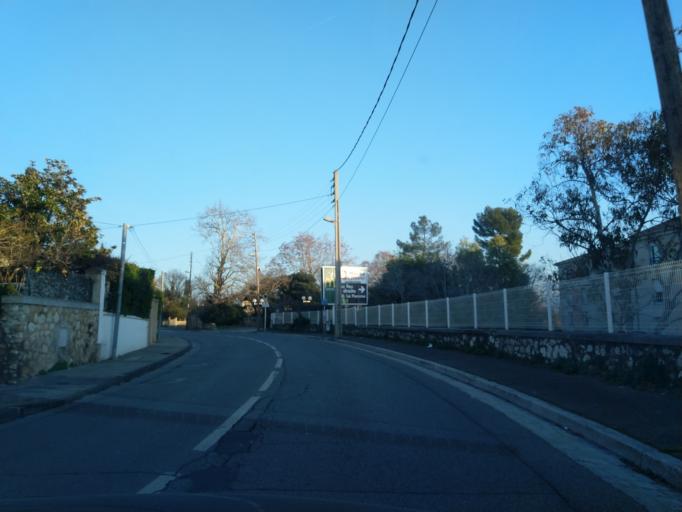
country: FR
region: Provence-Alpes-Cote d'Azur
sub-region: Departement des Bouches-du-Rhone
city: Marseille 12
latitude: 43.3039
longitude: 5.4355
